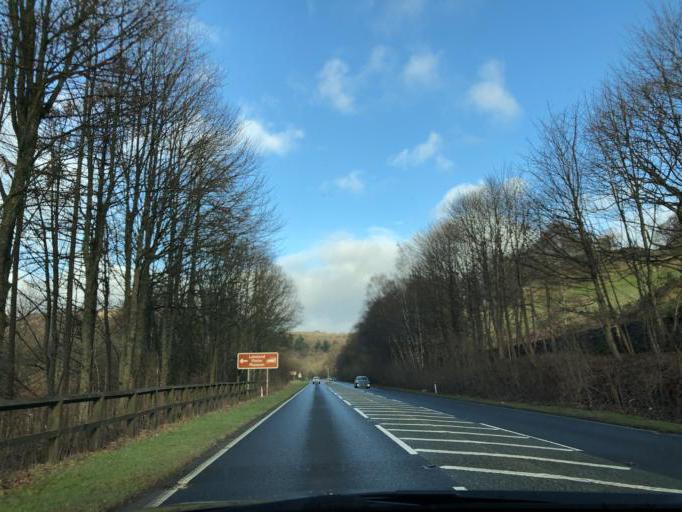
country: GB
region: England
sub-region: Cumbria
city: Grange-over-Sands
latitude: 54.2585
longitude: -2.9883
